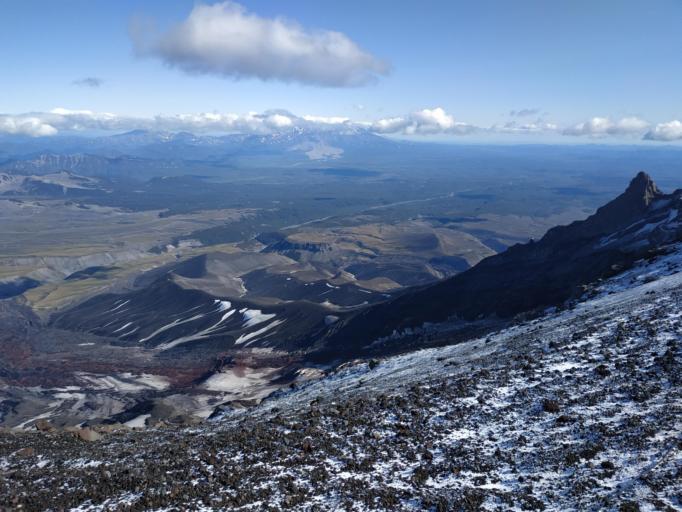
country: RU
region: Kamtsjatka
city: Petropavlovsk-Kamchatsky
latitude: 53.2666
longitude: 158.8194
